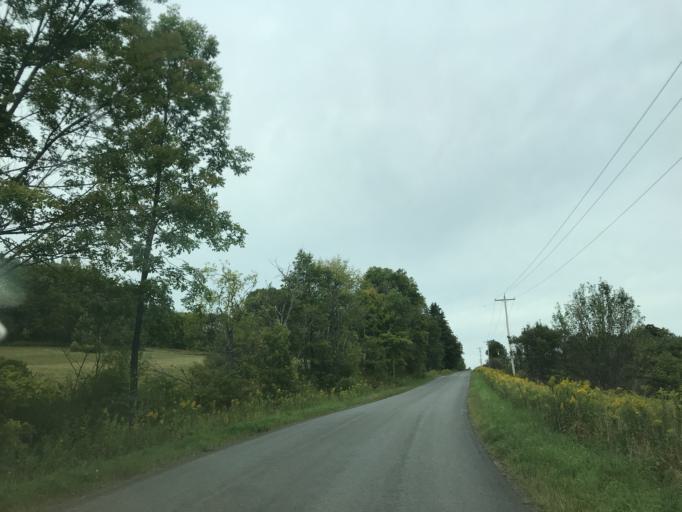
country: US
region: New York
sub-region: Otsego County
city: Worcester
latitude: 42.5674
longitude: -74.6707
